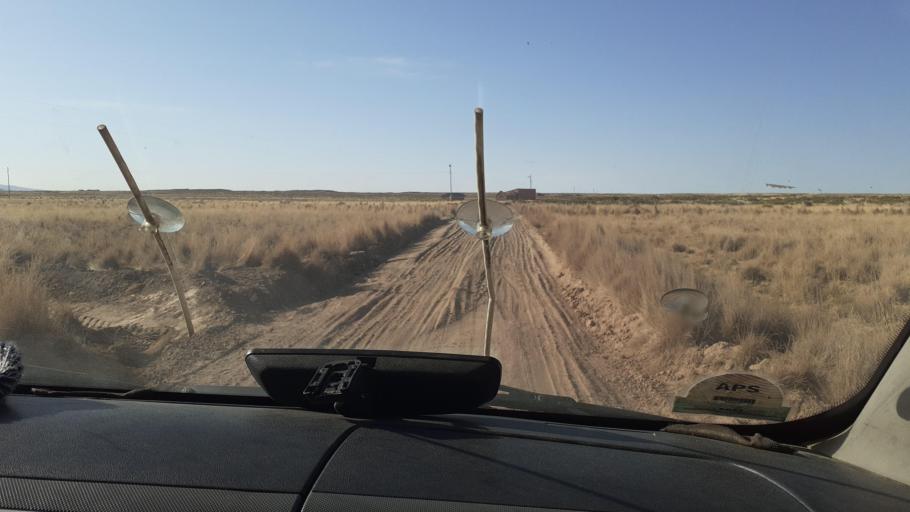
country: BO
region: La Paz
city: Tiahuanaco
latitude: -17.0824
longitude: -68.7599
